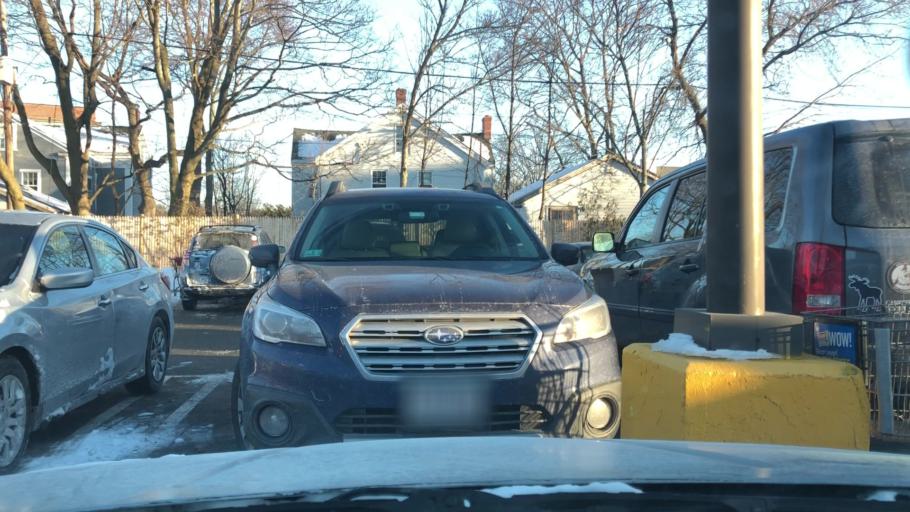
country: US
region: Massachusetts
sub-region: Middlesex County
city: Arlington
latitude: 42.4181
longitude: -71.1638
